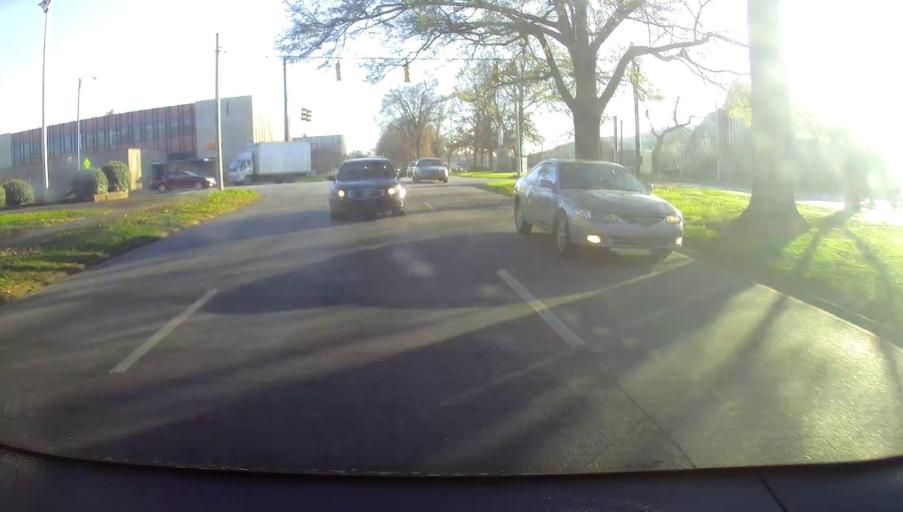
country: US
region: Alabama
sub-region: Calhoun County
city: Anniston
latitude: 33.6588
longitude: -85.8266
